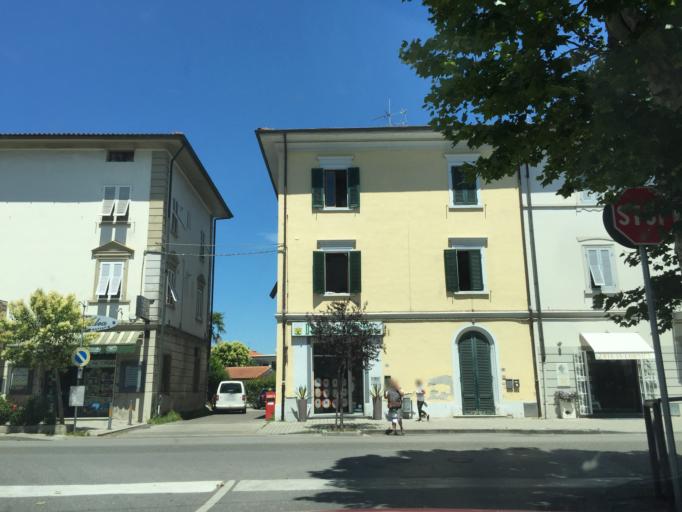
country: IT
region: Tuscany
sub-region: Province of Pisa
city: San Miniato
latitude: 43.6867
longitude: 10.7961
